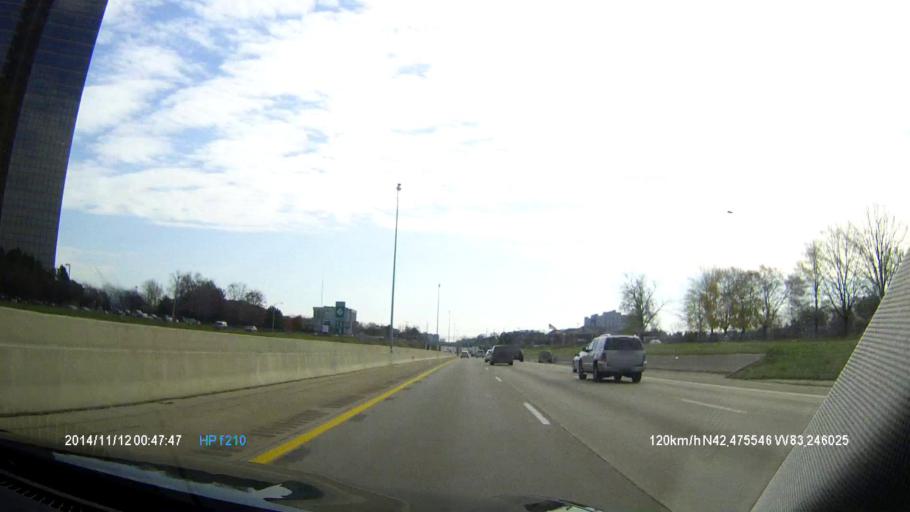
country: US
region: Michigan
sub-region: Oakland County
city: Southfield
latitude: 42.4755
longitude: -83.2459
